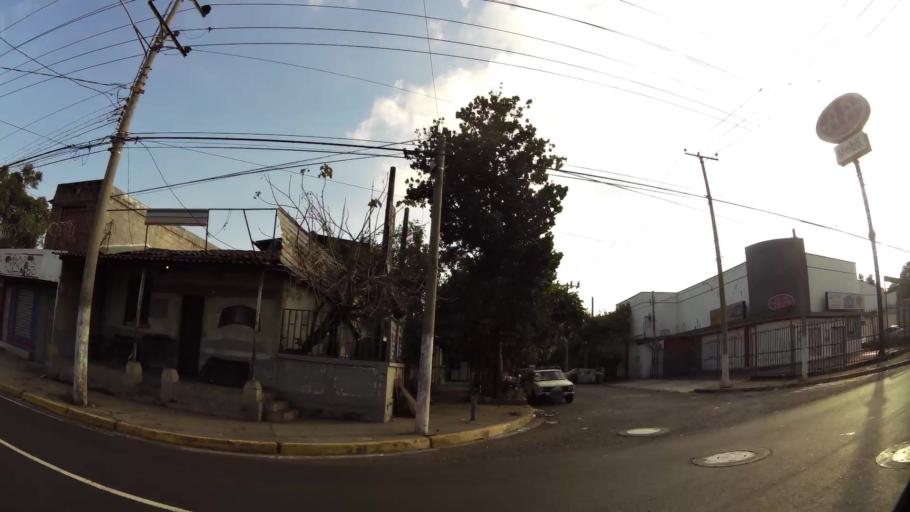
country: SV
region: San Salvador
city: San Salvador
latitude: 13.6917
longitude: -89.2142
